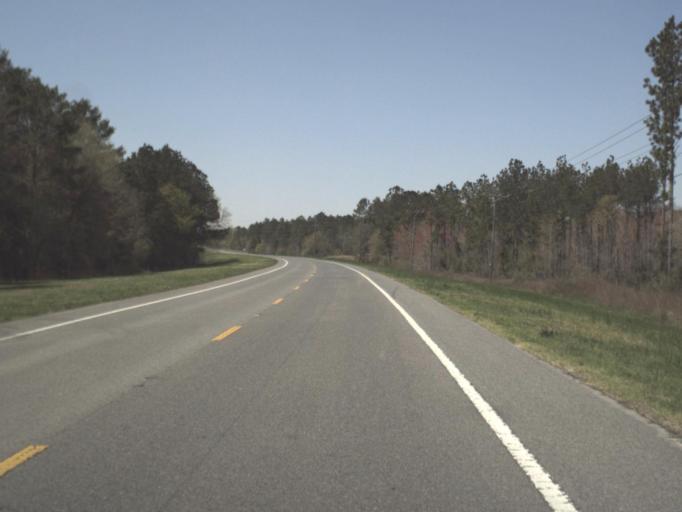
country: US
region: Alabama
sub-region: Geneva County
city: Geneva
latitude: 30.9485
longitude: -85.8331
